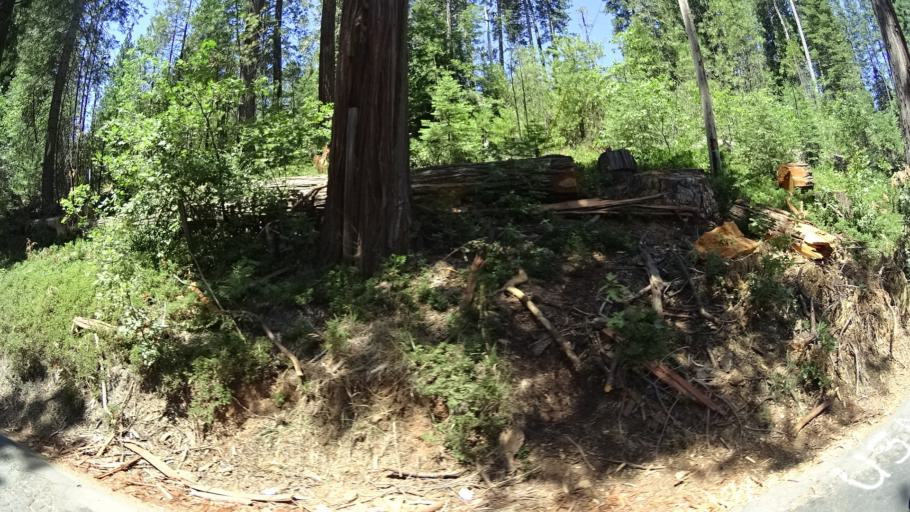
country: US
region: California
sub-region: Calaveras County
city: Arnold
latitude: 38.2174
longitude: -120.3584
